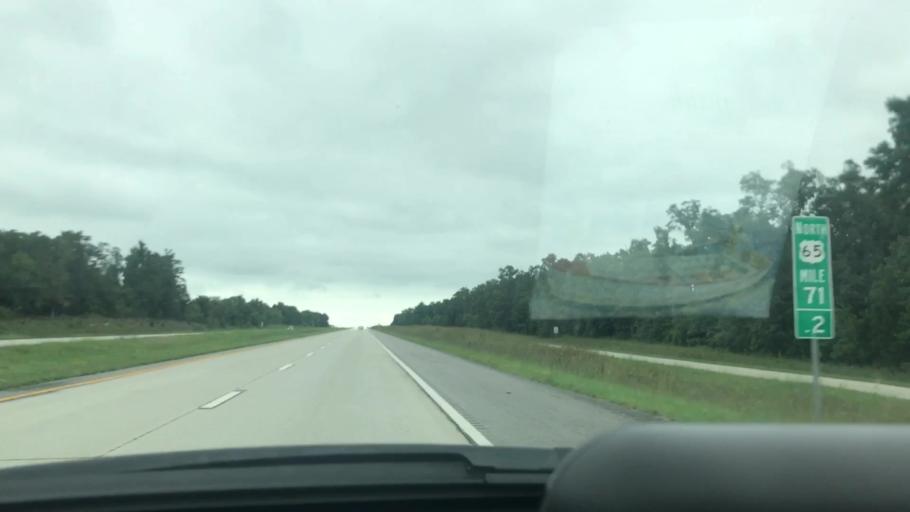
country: US
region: Missouri
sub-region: Greene County
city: Fair Grove
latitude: 37.4745
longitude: -93.1394
